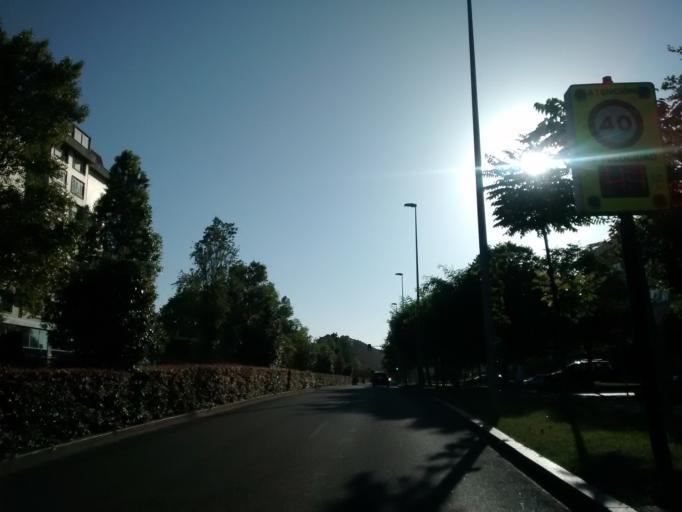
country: ES
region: Cantabria
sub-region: Provincia de Cantabria
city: Santander
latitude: 43.4716
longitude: -3.7973
